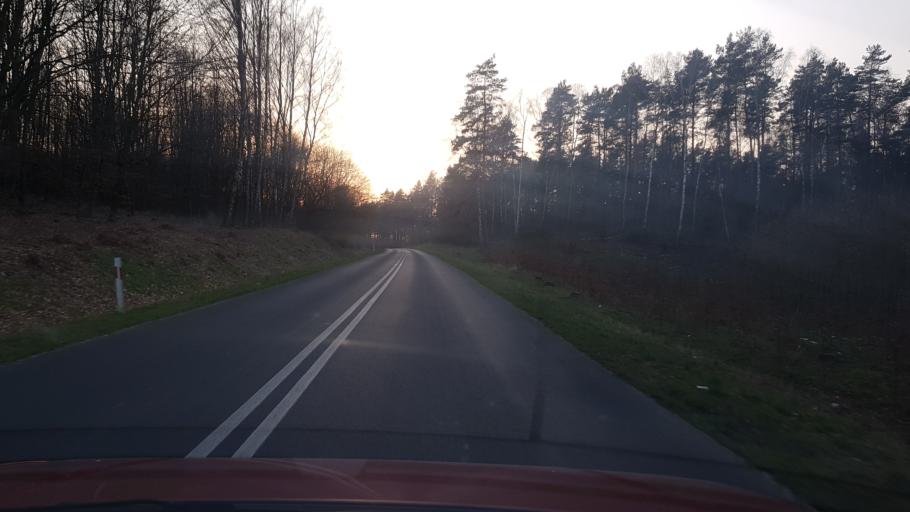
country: PL
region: West Pomeranian Voivodeship
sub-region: Powiat lobeski
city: Radowo Male
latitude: 53.6649
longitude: 15.4813
